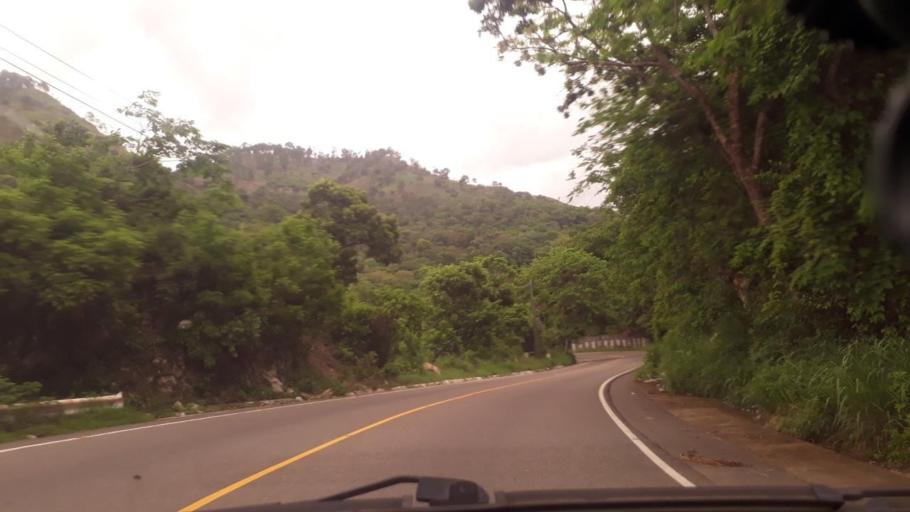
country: GT
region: Chiquimula
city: San Jacinto
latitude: 14.6571
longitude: -89.4905
